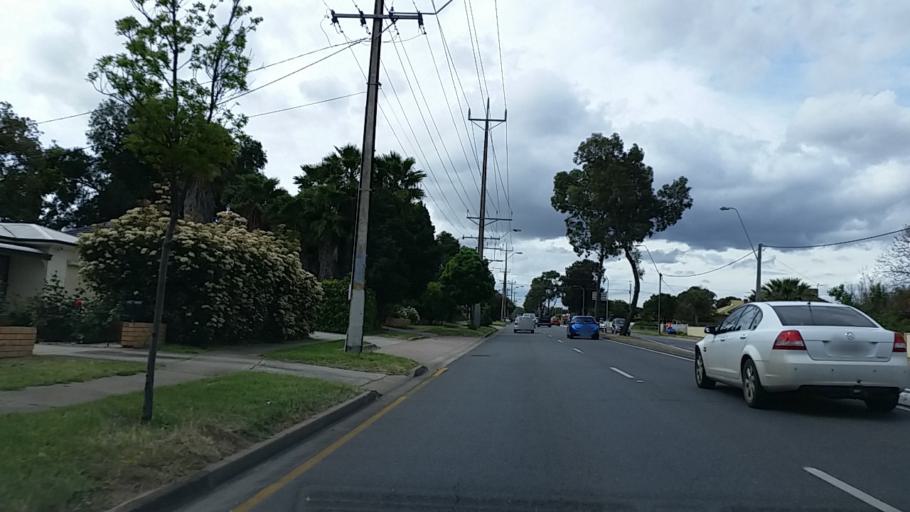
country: AU
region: South Australia
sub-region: Salisbury
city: Salisbury
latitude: -34.7691
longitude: 138.6353
